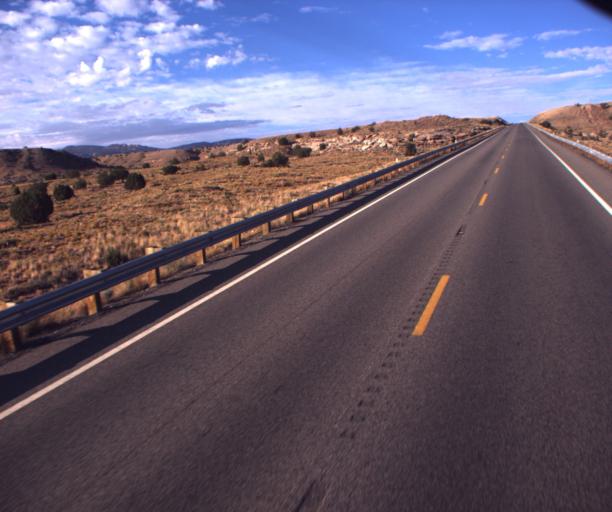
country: US
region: New Mexico
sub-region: San Juan County
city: Shiprock
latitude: 36.9301
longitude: -109.1541
